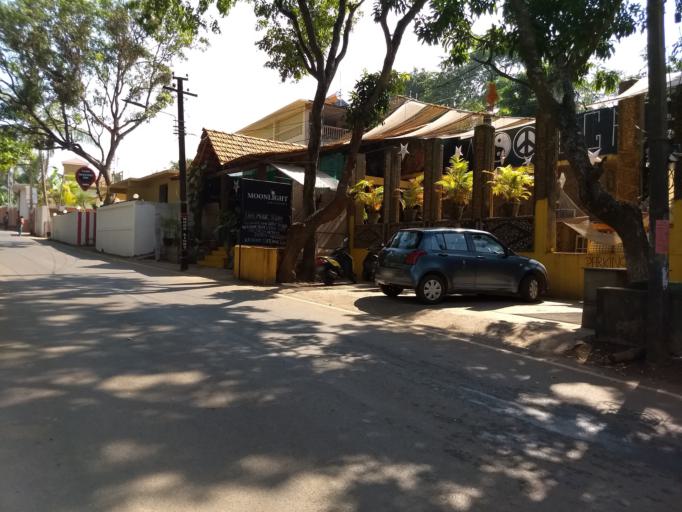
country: IN
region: Goa
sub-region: North Goa
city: Vagator
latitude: 15.5996
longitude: 73.7389
